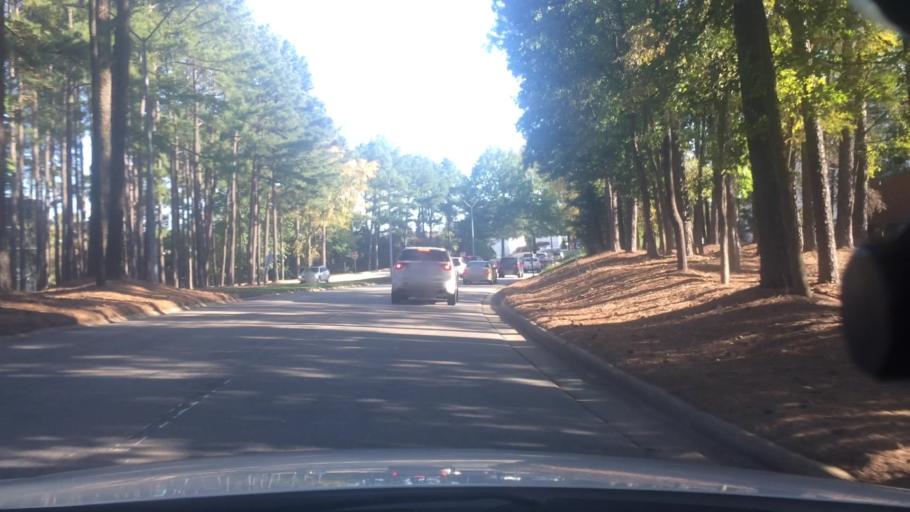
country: US
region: North Carolina
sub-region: Wake County
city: Raleigh
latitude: 35.8190
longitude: -78.6016
